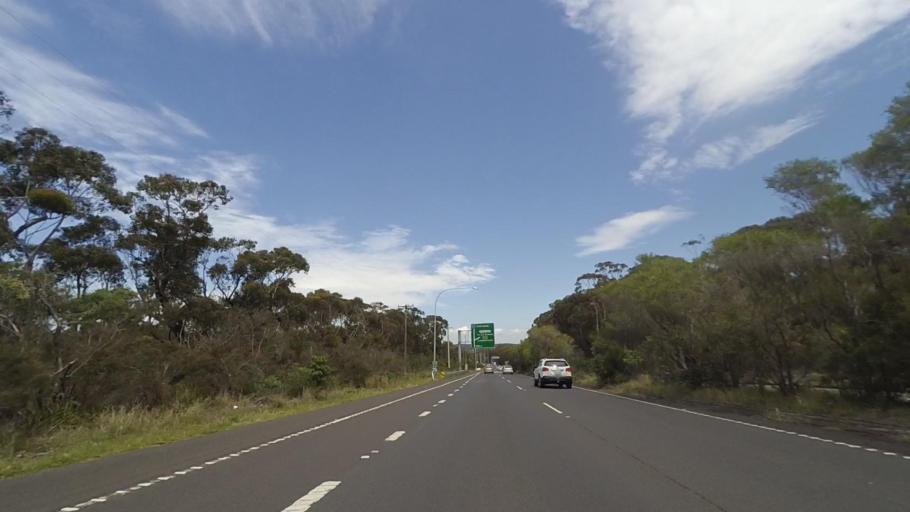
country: AU
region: New South Wales
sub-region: Wollongong
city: Bulli
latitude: -34.3008
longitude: 150.9122
